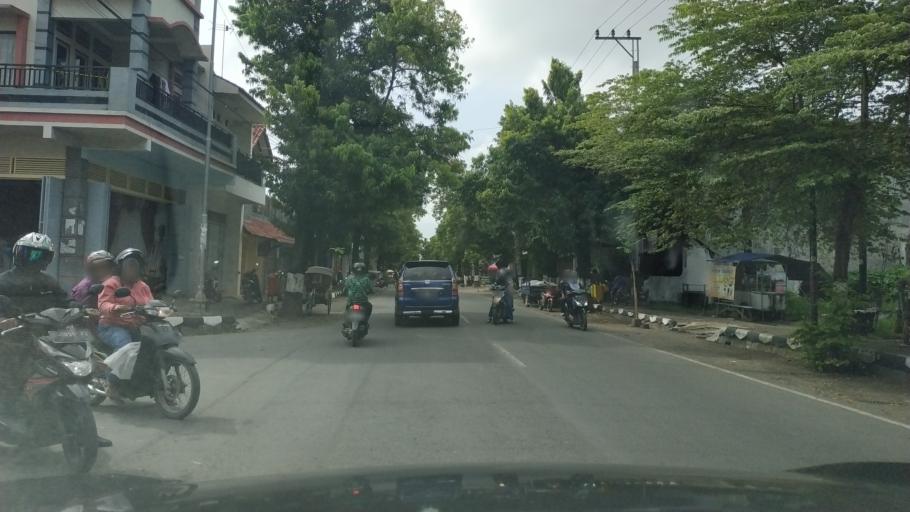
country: ID
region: Central Java
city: Pemalang
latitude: -6.8951
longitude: 109.3829
